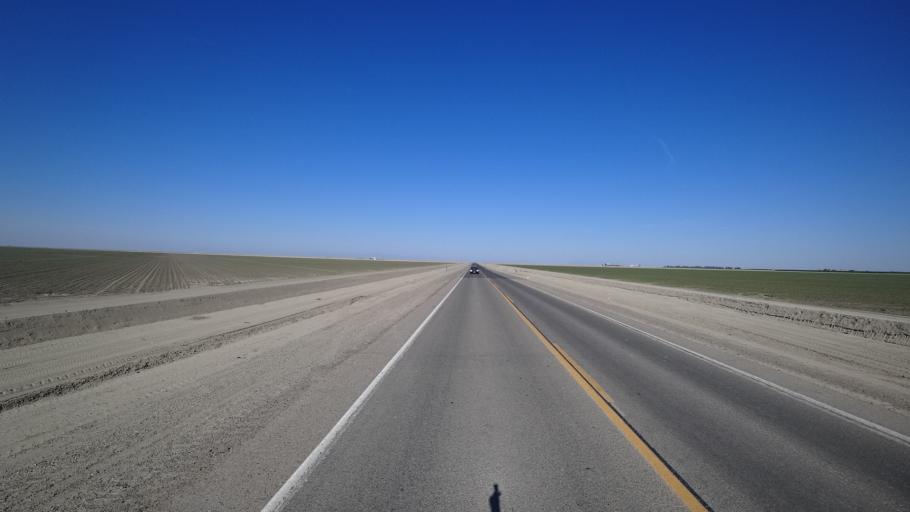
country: US
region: California
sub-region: Kings County
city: Corcoran
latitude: 36.0980
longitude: -119.6088
